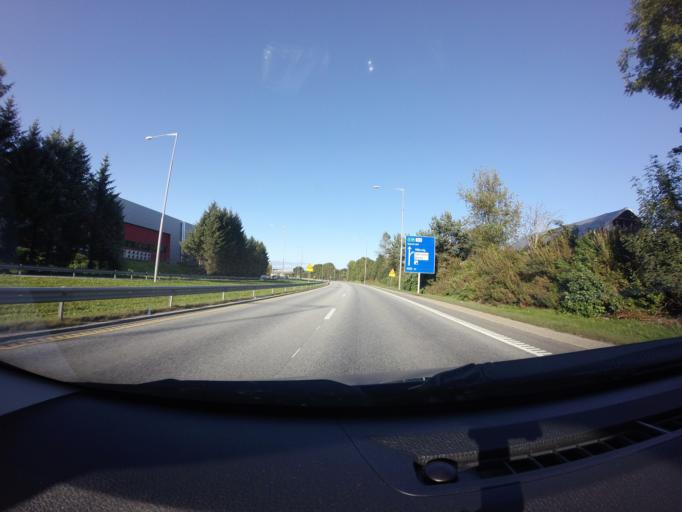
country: NO
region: Rogaland
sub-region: Stavanger
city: Stavanger
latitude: 58.9384
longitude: 5.7227
